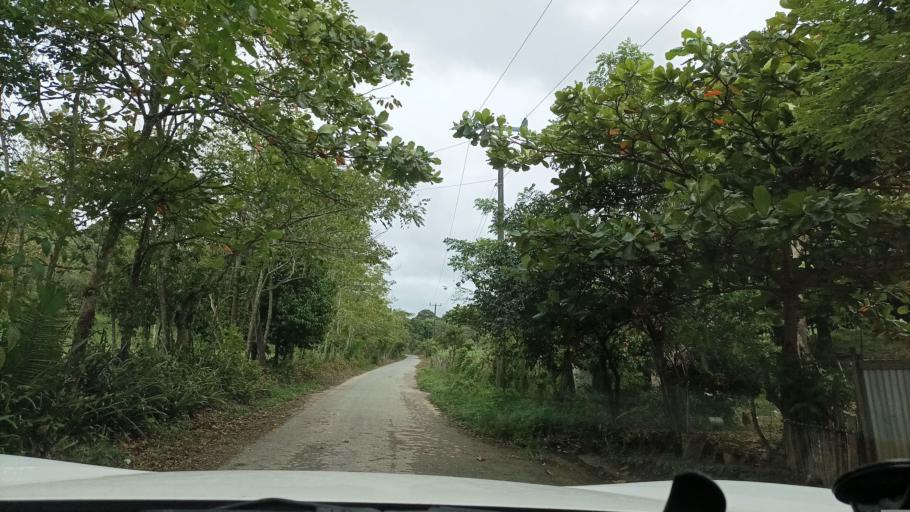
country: MX
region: Veracruz
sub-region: Moloacan
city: Cuichapa
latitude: 17.8531
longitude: -94.3555
